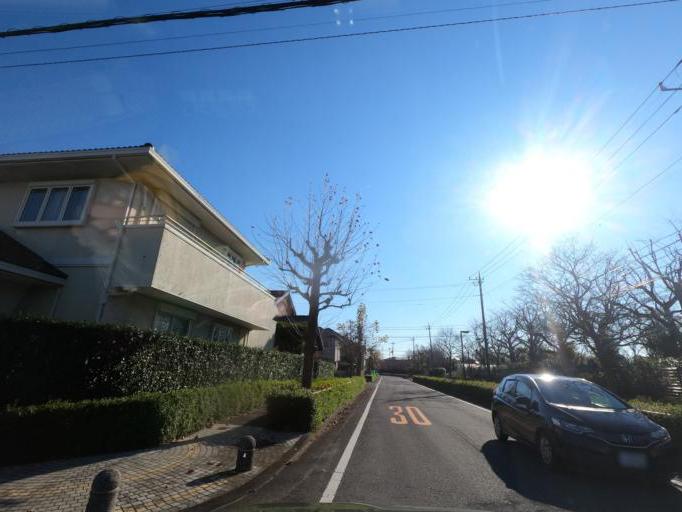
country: JP
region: Ibaraki
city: Mitsukaido
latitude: 35.9747
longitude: 139.9750
